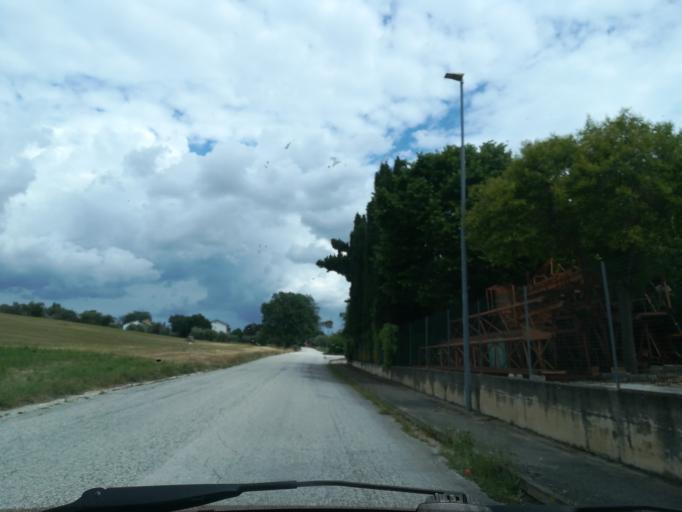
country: IT
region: The Marches
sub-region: Provincia di Macerata
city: Petriolo
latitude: 43.2257
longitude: 13.4749
